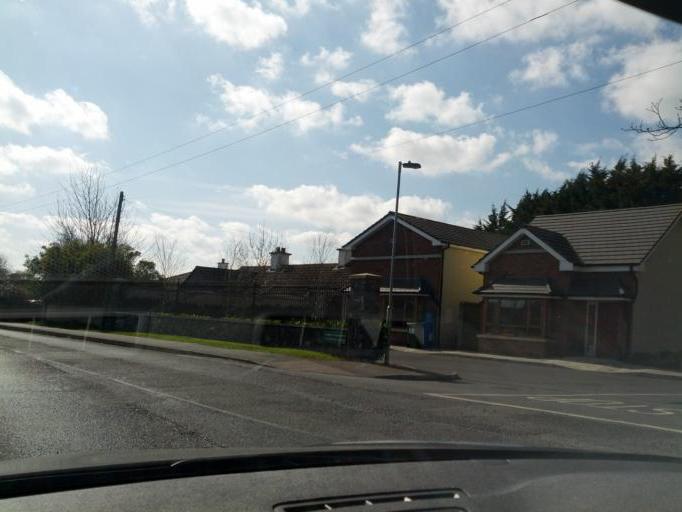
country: IE
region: Leinster
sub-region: Kildare
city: Leixlip
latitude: 53.3610
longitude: -6.5027
